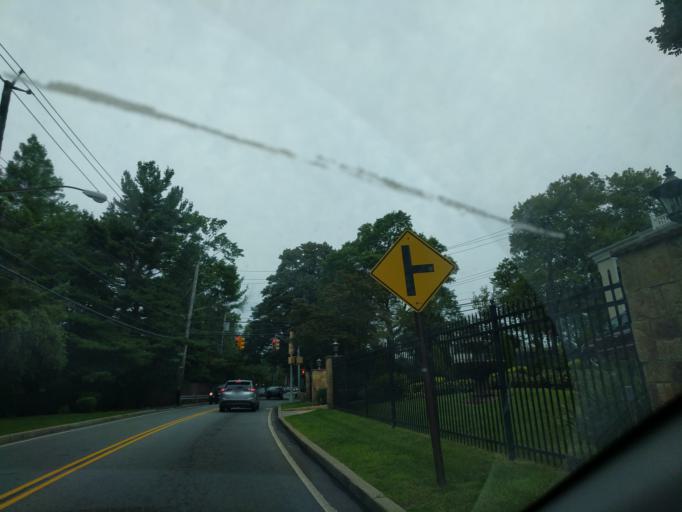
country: US
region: New York
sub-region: Richmond County
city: Staten Island
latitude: 40.5928
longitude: -74.1107
